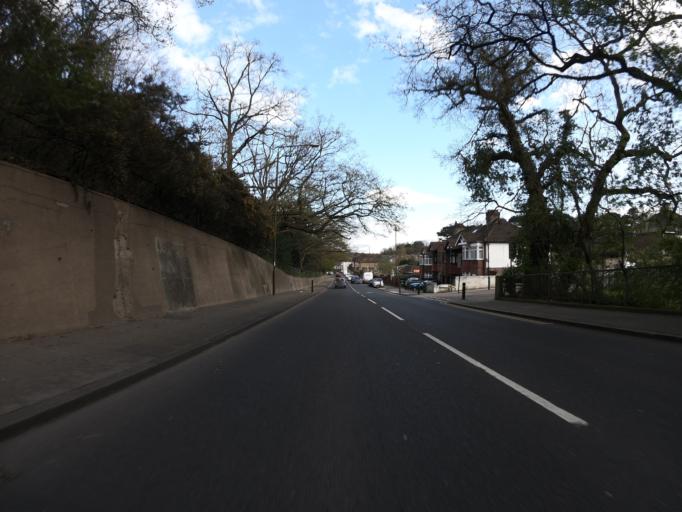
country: GB
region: England
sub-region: Greater London
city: Abbey Wood
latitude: 51.4795
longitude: 0.0983
